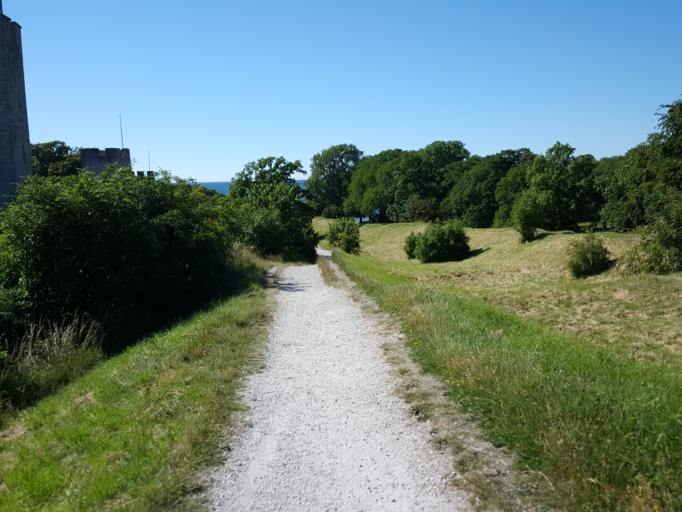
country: SE
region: Gotland
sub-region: Gotland
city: Visby
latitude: 57.6458
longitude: 18.2994
